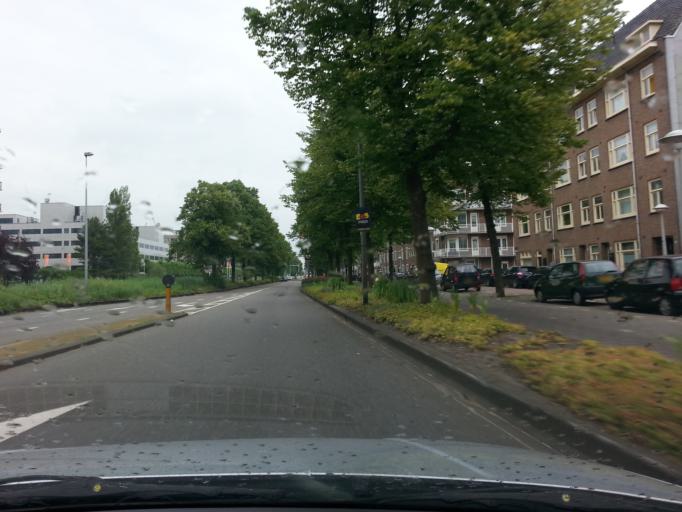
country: NL
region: North Holland
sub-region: Gemeente Amsterdam
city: Amsterdam
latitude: 52.3849
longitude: 4.8484
